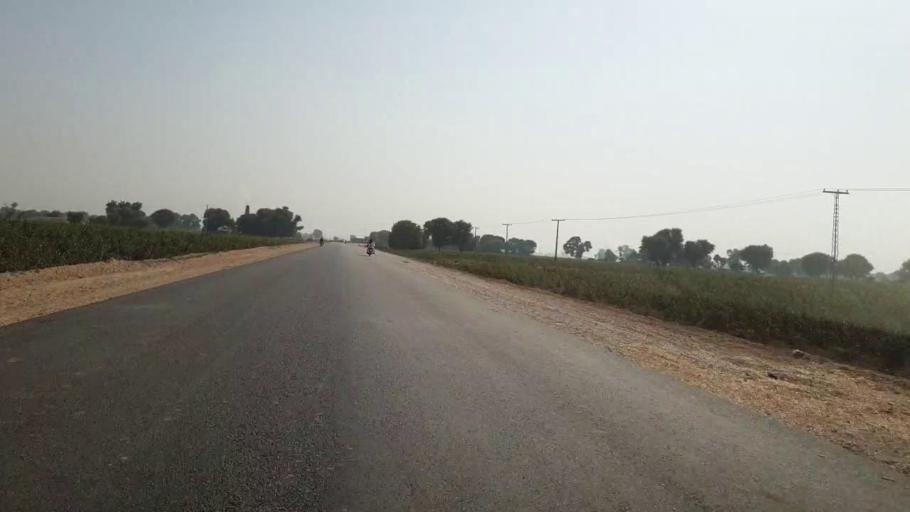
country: PK
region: Sindh
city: Dadu
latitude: 26.6794
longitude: 67.7766
